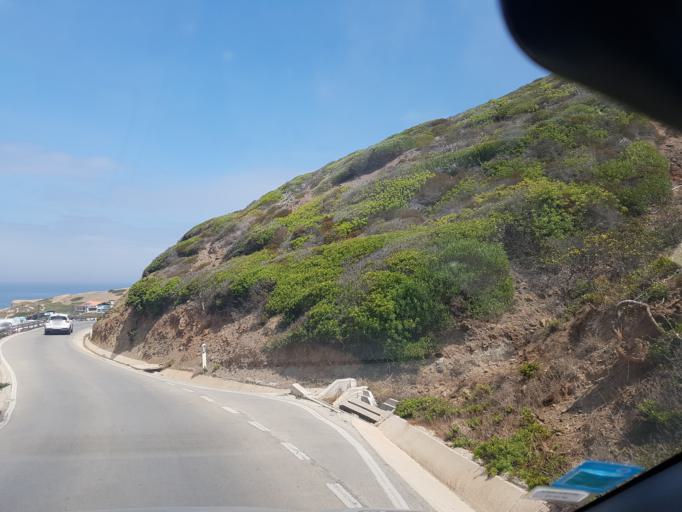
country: PT
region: Faro
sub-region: Vila do Bispo
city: Vila do Bispo
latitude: 37.1074
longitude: -8.9343
